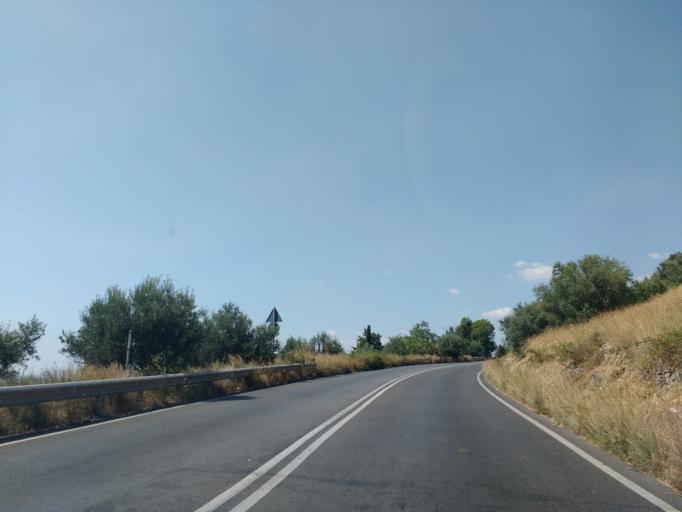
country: IT
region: Latium
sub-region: Citta metropolitana di Roma Capitale
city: Tivoli
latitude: 41.9501
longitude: 12.7911
